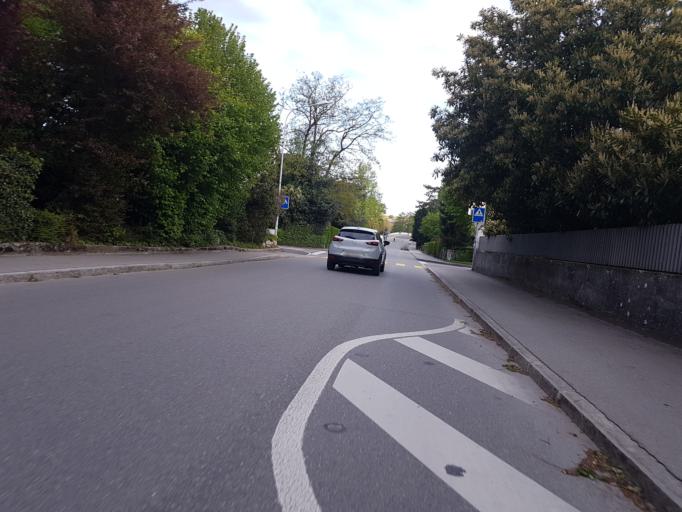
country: CH
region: Bern
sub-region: Biel/Bienne District
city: Nidau
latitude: 47.1249
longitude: 7.2368
